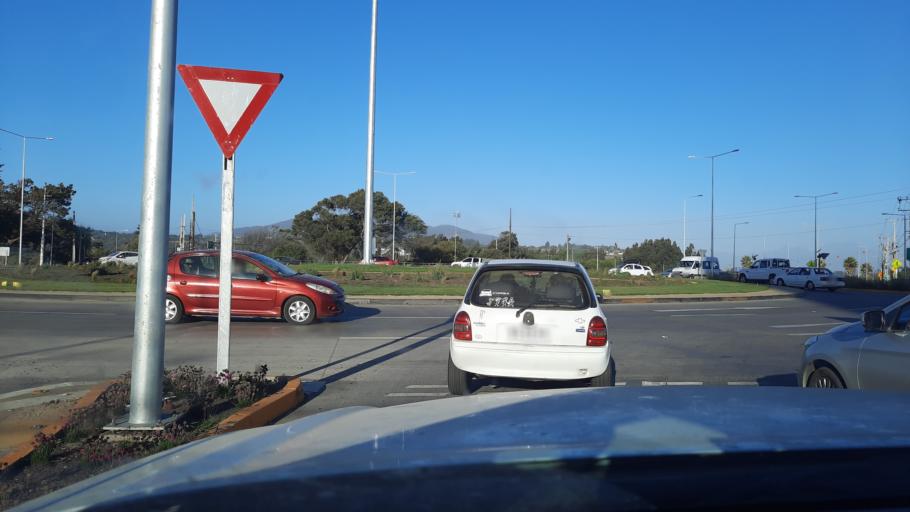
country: CL
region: Valparaiso
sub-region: Provincia de Valparaiso
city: Vina del Mar
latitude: -32.9217
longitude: -71.5073
